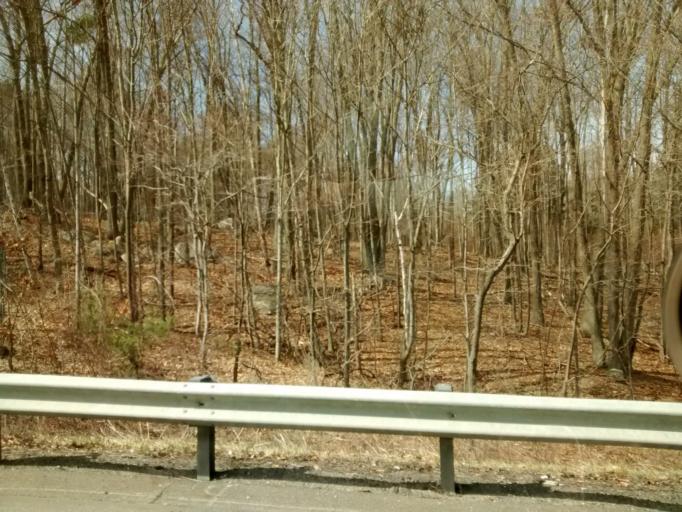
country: US
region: Massachusetts
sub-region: Worcester County
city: Charlton
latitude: 42.1432
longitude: -72.0208
